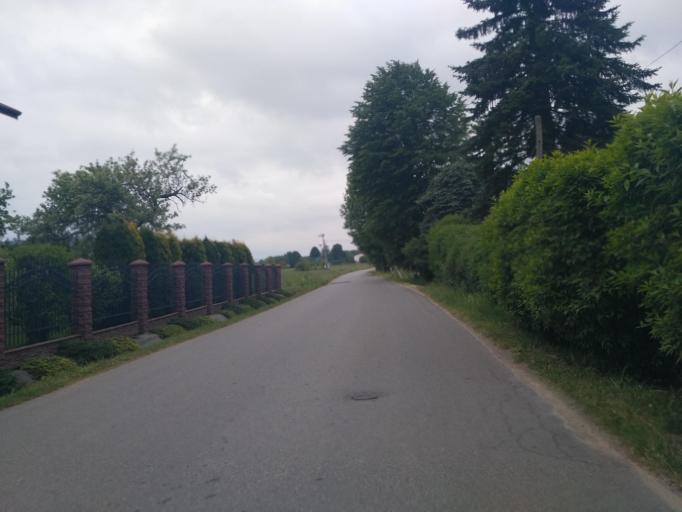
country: PL
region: Subcarpathian Voivodeship
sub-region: Krosno
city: Krosno
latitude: 49.6747
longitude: 21.7334
